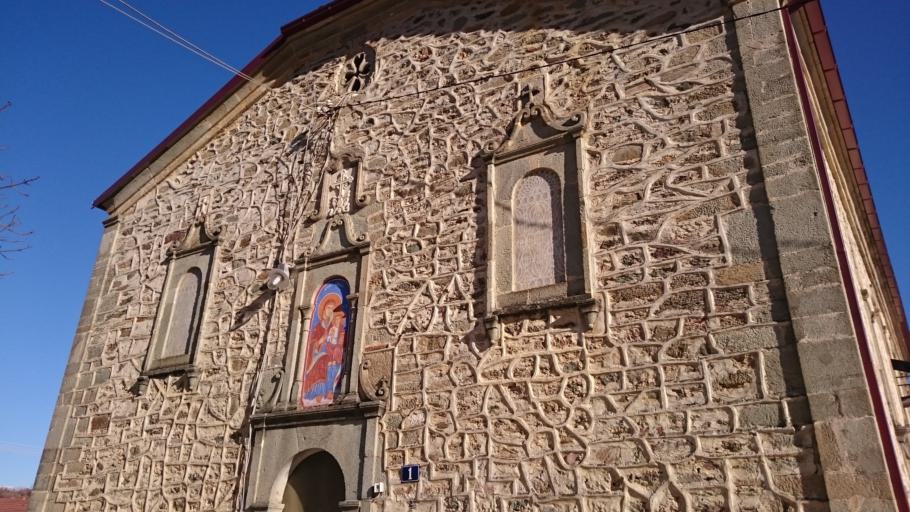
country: MK
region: Makedonski Brod
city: Makedonski Brod
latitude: 41.5136
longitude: 21.2139
